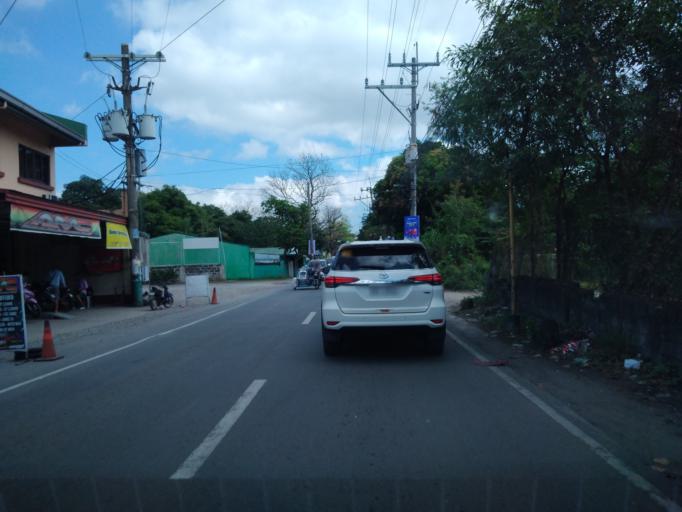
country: PH
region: Central Luzon
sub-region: Province of Bulacan
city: Santa Maria
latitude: 14.8257
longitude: 120.9696
